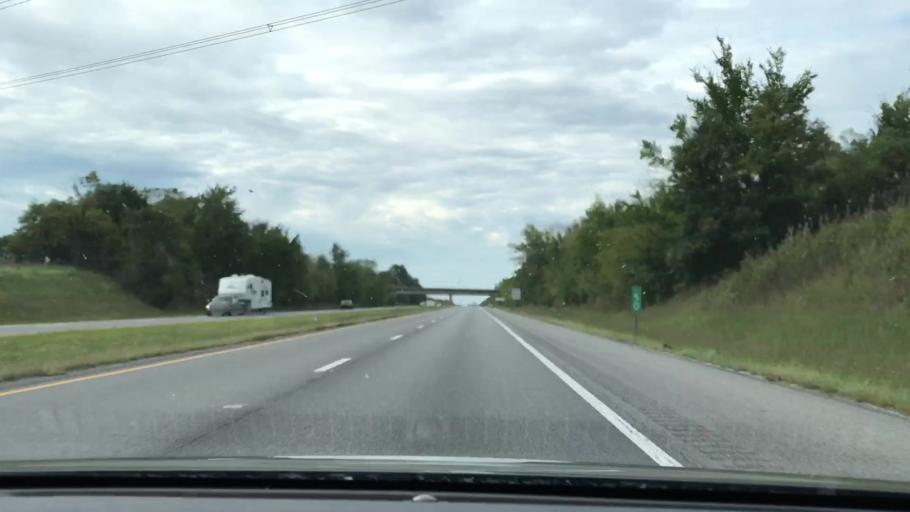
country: US
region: Kentucky
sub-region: Marshall County
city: Calvert City
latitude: 36.9715
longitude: -88.3468
